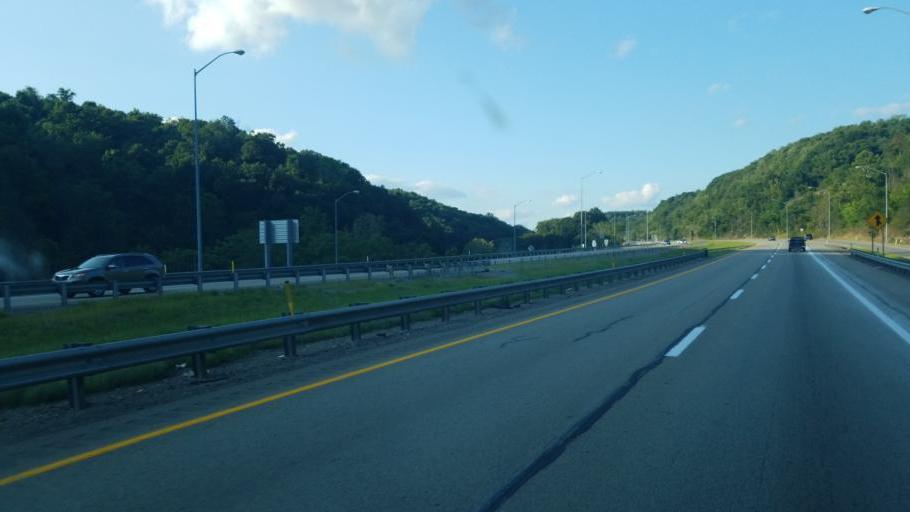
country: US
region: Pennsylvania
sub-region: Allegheny County
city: Coraopolis
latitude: 40.5287
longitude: -80.1290
